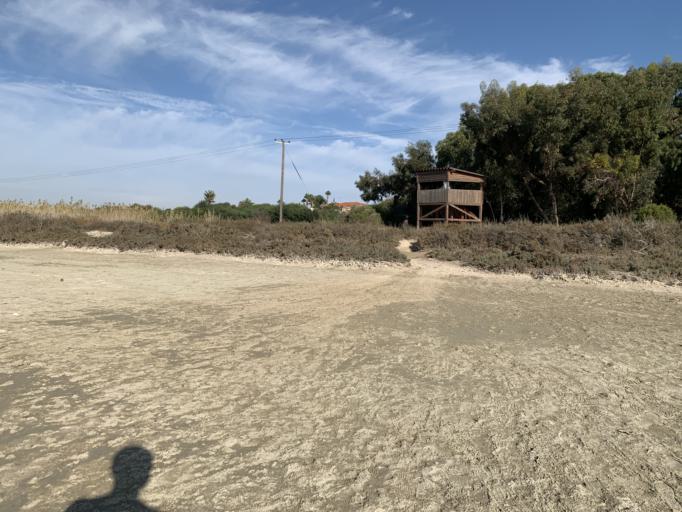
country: CY
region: Larnaka
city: Larnaca
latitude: 34.9056
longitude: 33.6202
